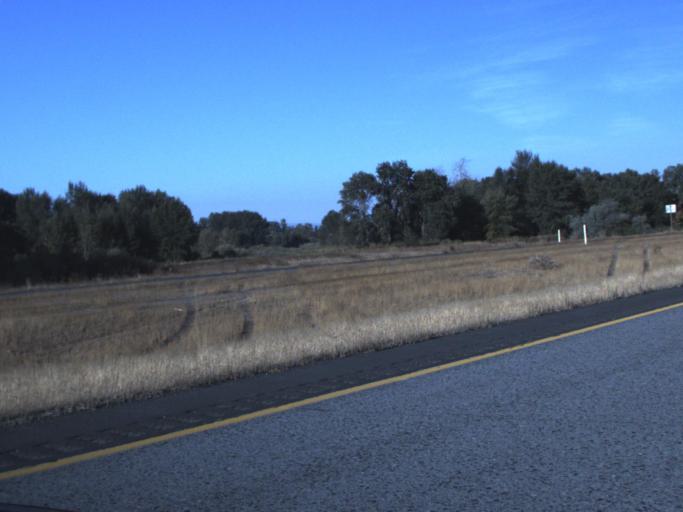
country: US
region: Washington
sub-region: Yakima County
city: Wapato
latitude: 46.4655
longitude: -120.3828
